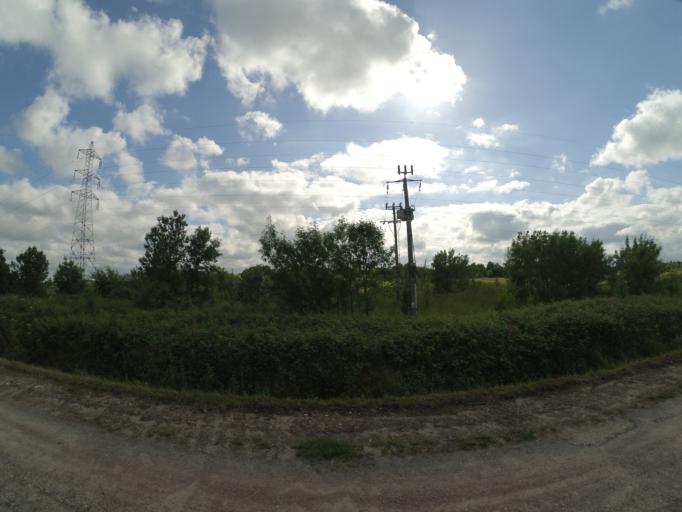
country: FR
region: Aquitaine
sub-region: Departement de la Gironde
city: Bassens
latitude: 44.9044
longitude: -0.5544
